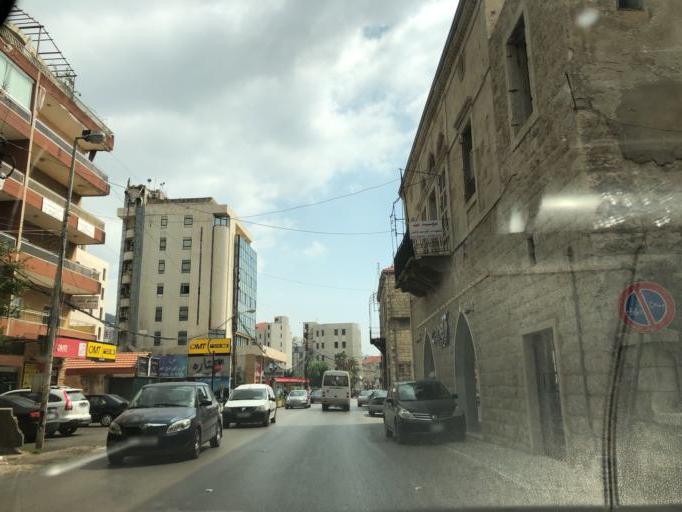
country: LB
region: Mont-Liban
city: Djounie
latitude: 33.9892
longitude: 35.6382
